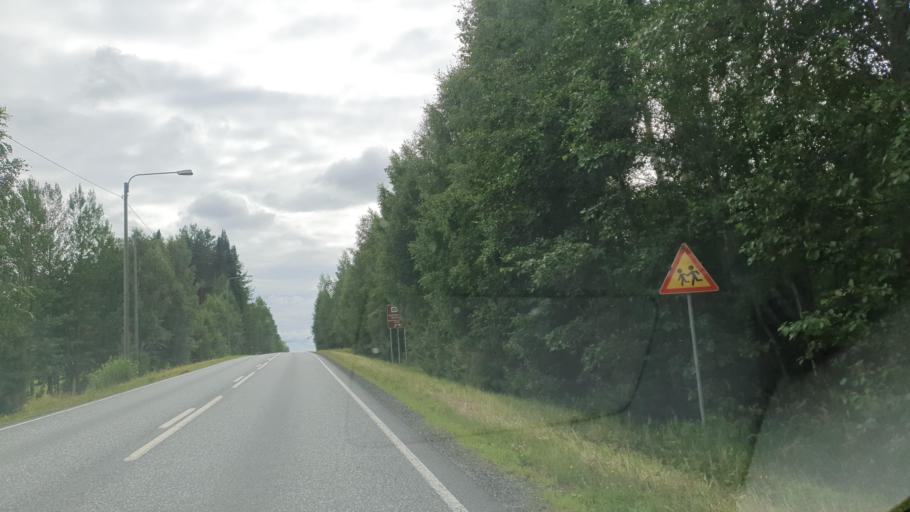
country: FI
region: Northern Savo
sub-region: Ylae-Savo
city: Iisalmi
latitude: 63.5155
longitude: 27.1254
